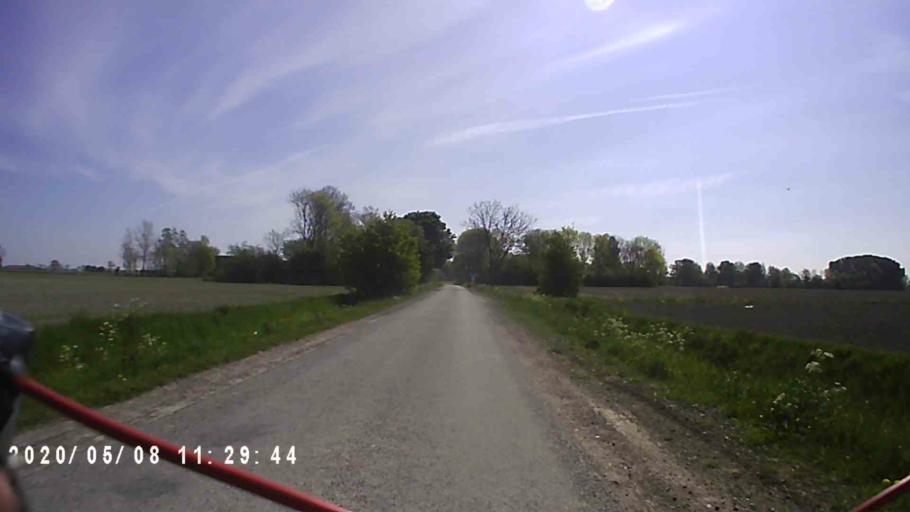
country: NL
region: Groningen
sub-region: Gemeente Bedum
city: Bedum
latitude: 53.3461
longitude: 6.7030
